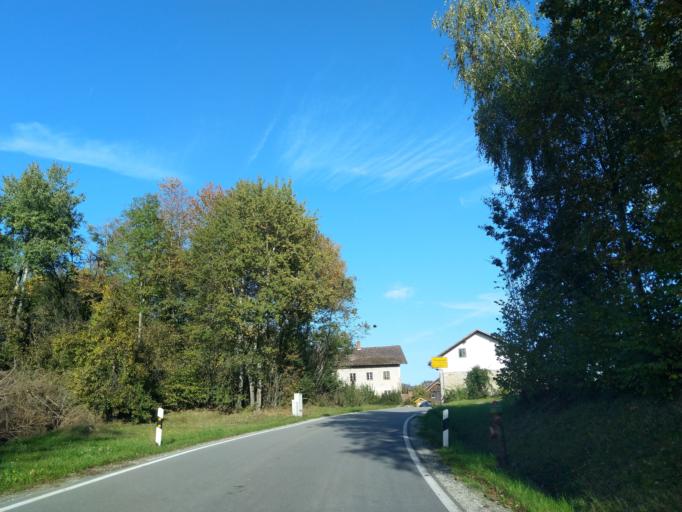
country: DE
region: Bavaria
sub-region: Lower Bavaria
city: Offenberg
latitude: 48.8934
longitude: 12.8485
